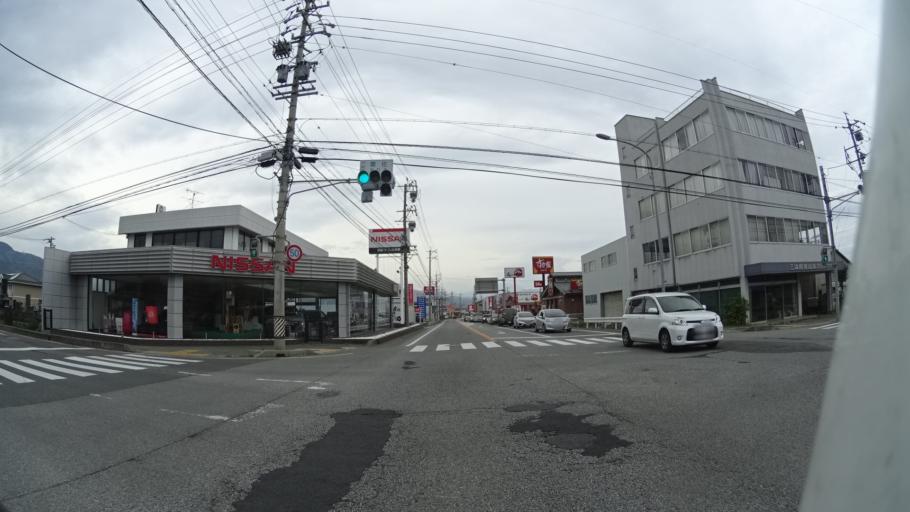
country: JP
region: Nagano
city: Nagano-shi
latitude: 36.5380
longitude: 138.1226
